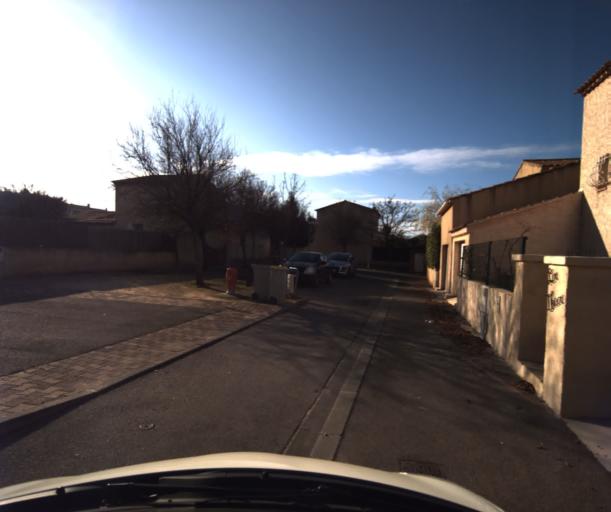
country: FR
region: Provence-Alpes-Cote d'Azur
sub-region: Departement du Vaucluse
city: Pertuis
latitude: 43.6933
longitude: 5.5231
